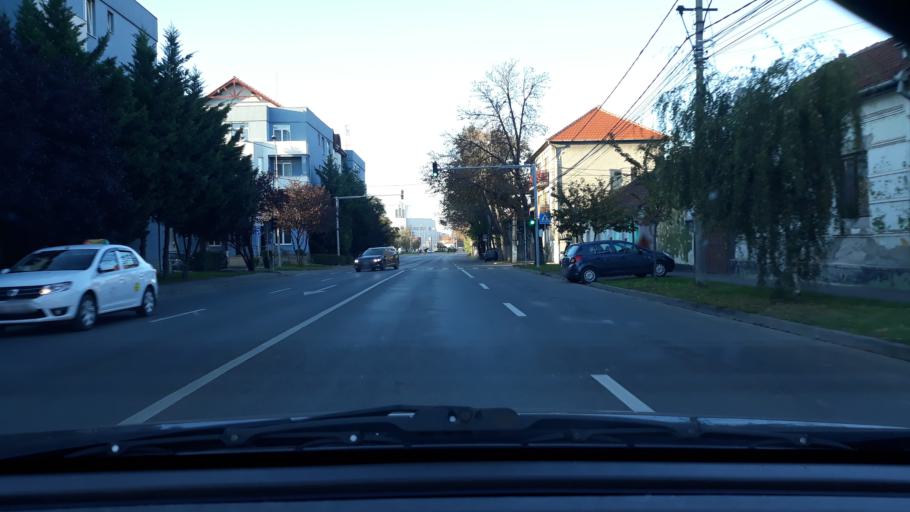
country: RO
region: Bihor
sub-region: Comuna Biharea
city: Oradea
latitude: 47.0530
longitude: 21.9188
